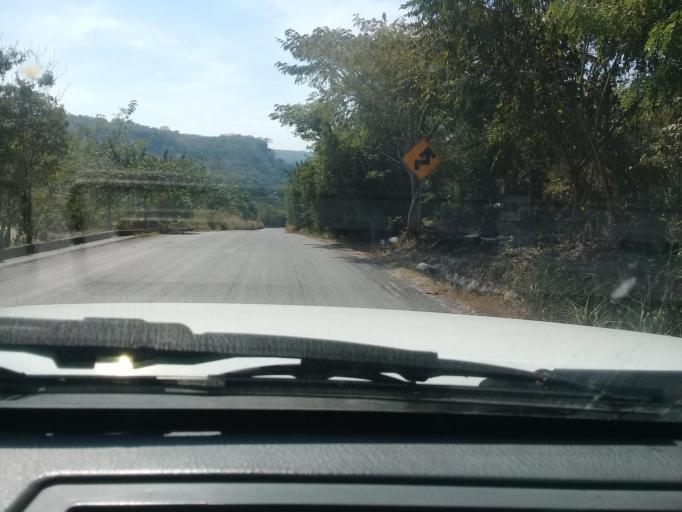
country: MX
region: Veracruz
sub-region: Emiliano Zapata
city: Plan del Rio
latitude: 19.4270
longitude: -96.6074
